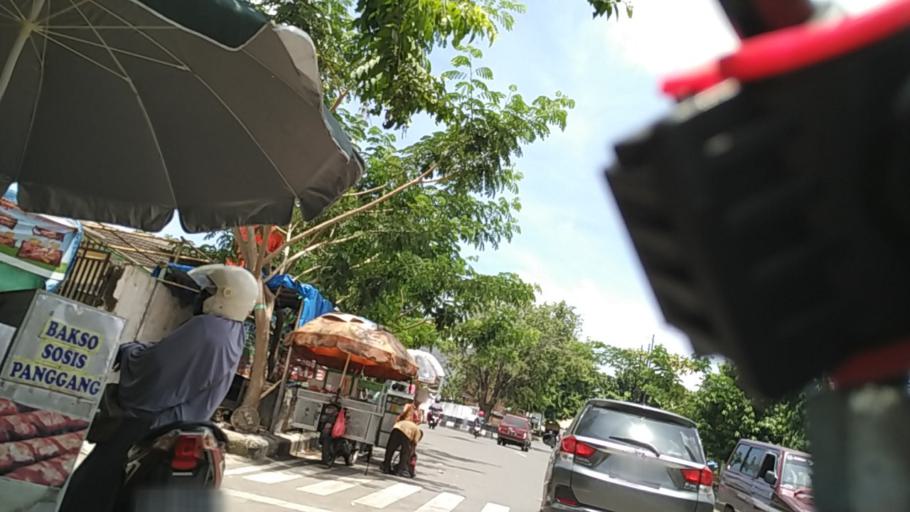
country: ID
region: Central Java
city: Semarang
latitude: -6.9997
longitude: 110.3892
